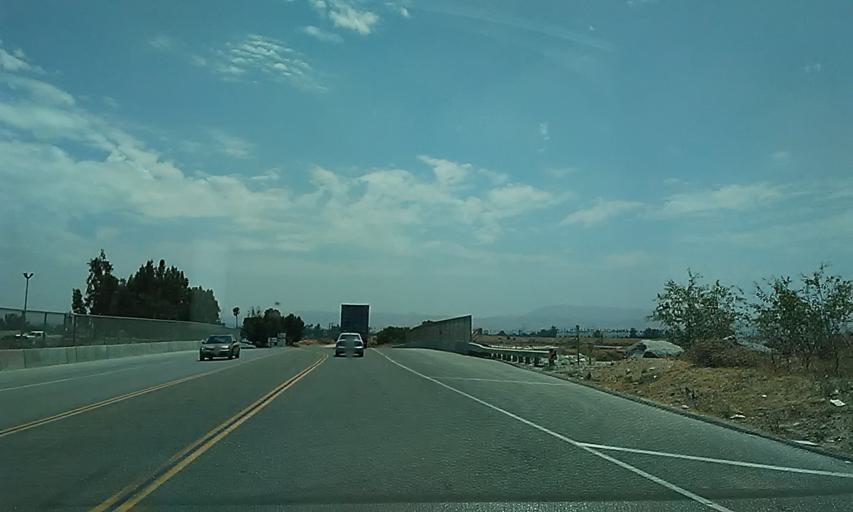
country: US
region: California
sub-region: San Bernardino County
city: Highland
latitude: 34.1032
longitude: -117.2089
